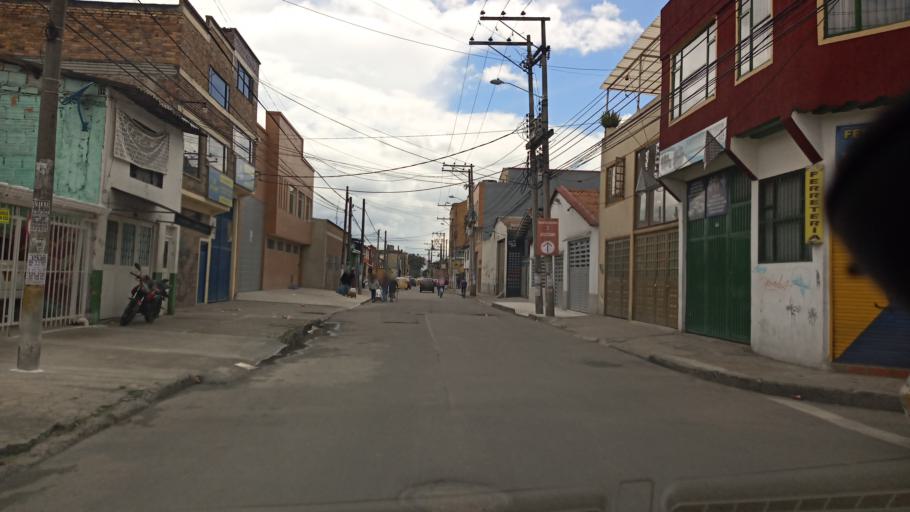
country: CO
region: Cundinamarca
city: Funza
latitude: 4.6720
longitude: -74.1426
